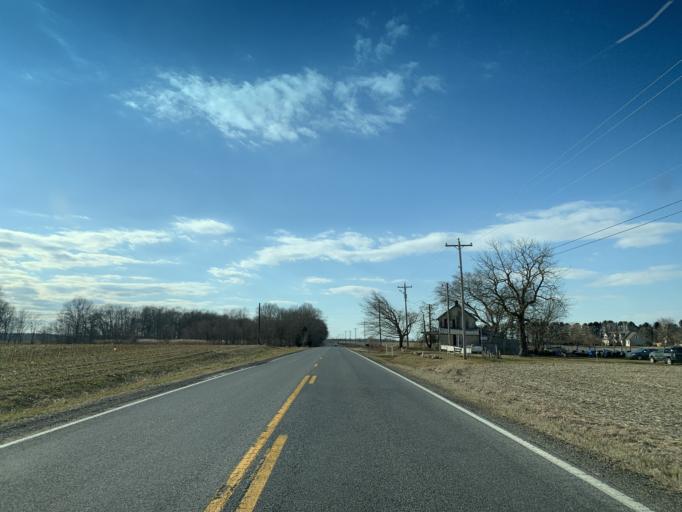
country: US
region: Maryland
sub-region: Queen Anne's County
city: Centreville
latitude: 39.0046
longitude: -75.9755
